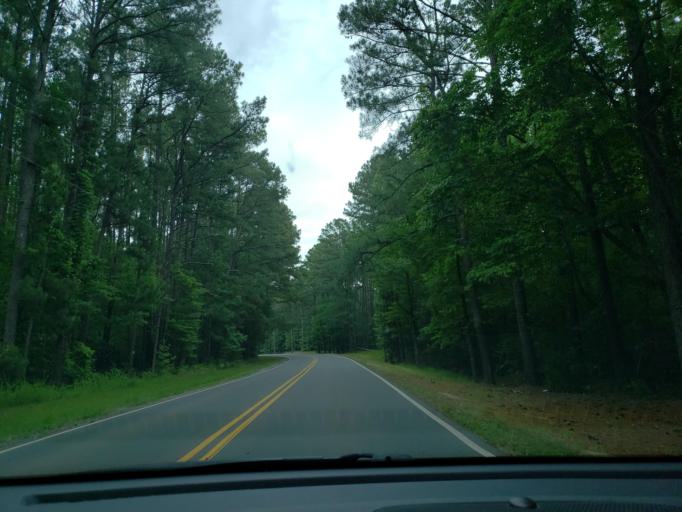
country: US
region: North Carolina
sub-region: Chatham County
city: Fearrington Village
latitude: 35.7132
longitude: -79.0110
